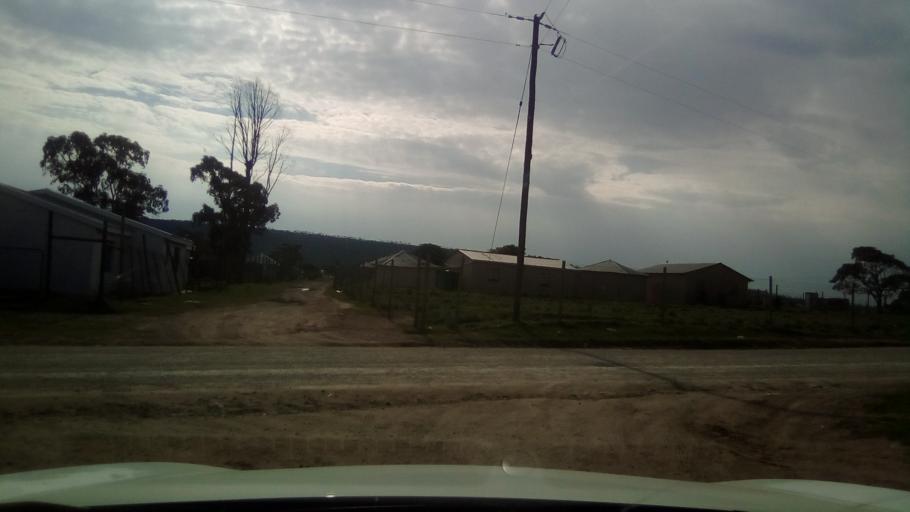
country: ZA
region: Eastern Cape
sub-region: Buffalo City Metropolitan Municipality
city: Bhisho
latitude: -32.9861
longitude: 27.2725
